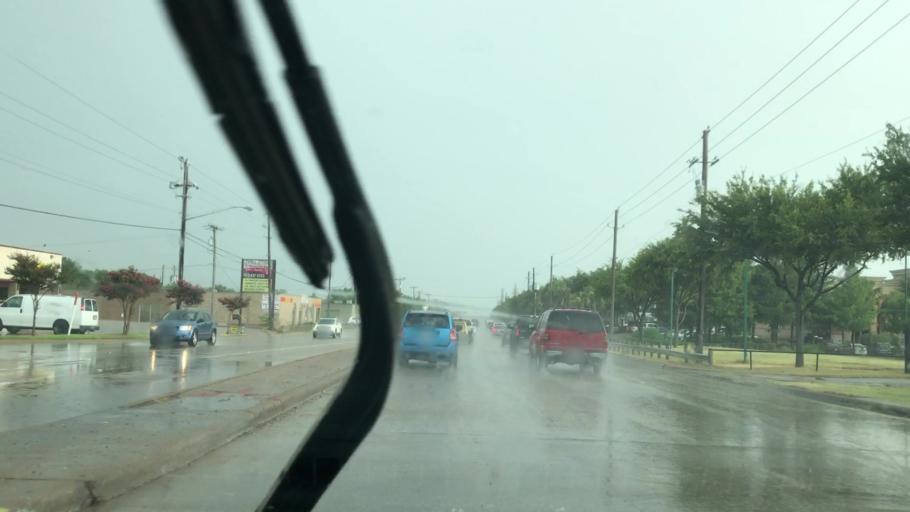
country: US
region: Texas
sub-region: Dallas County
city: Richardson
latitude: 32.8944
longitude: -96.7004
